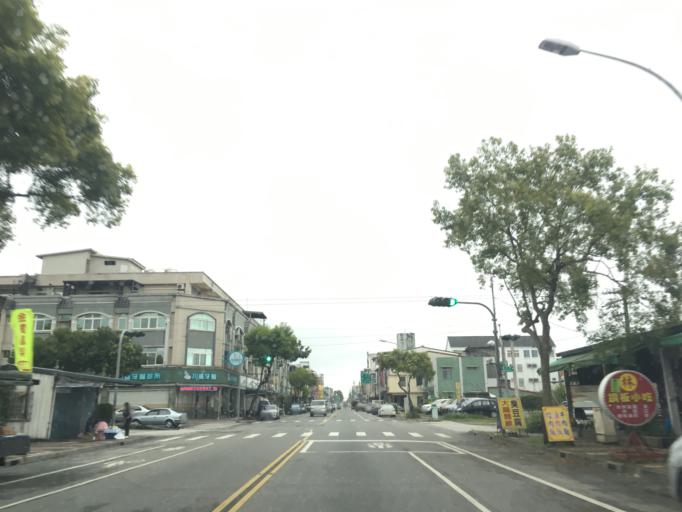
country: TW
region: Taiwan
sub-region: Hualien
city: Hualian
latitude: 23.9776
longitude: 121.5659
